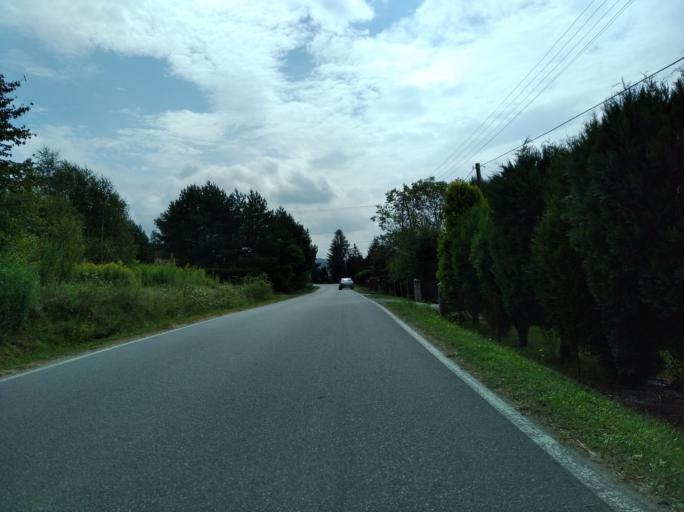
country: PL
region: Subcarpathian Voivodeship
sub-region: Powiat krosnienski
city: Leki
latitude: 49.7991
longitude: 21.6765
